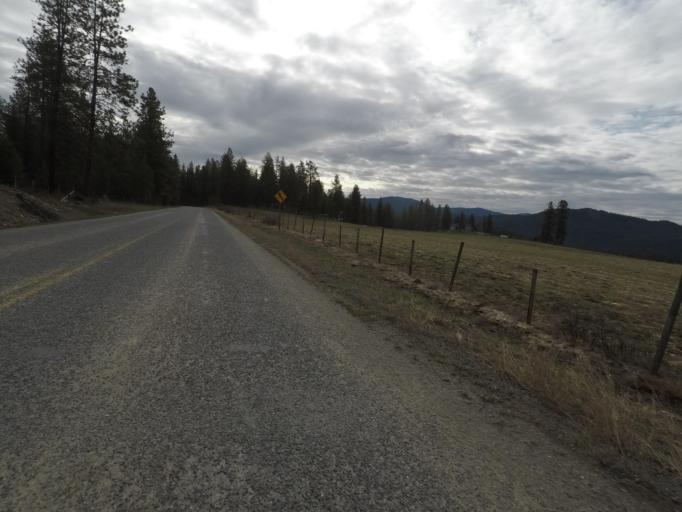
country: US
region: Washington
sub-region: Stevens County
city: Colville
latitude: 48.4984
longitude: -117.8398
